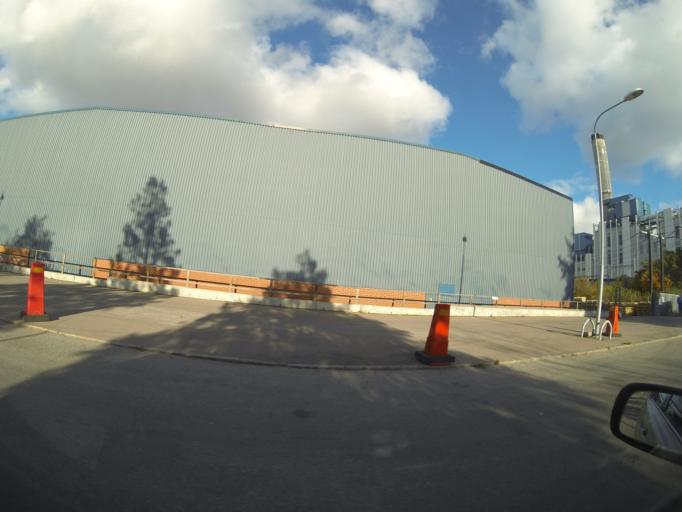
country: SE
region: Vaestmanland
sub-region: Vasteras
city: Vasteras
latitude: 59.5889
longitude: 16.5091
